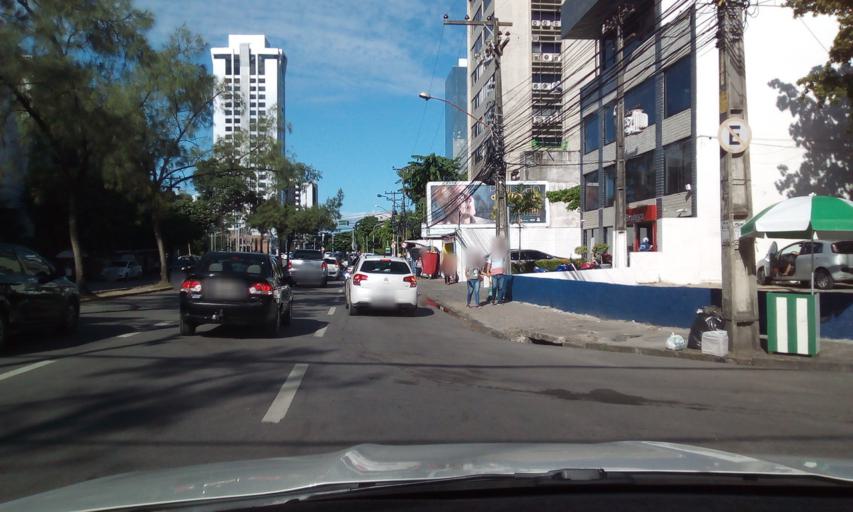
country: BR
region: Pernambuco
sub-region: Recife
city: Recife
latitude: -8.0623
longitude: -34.8989
